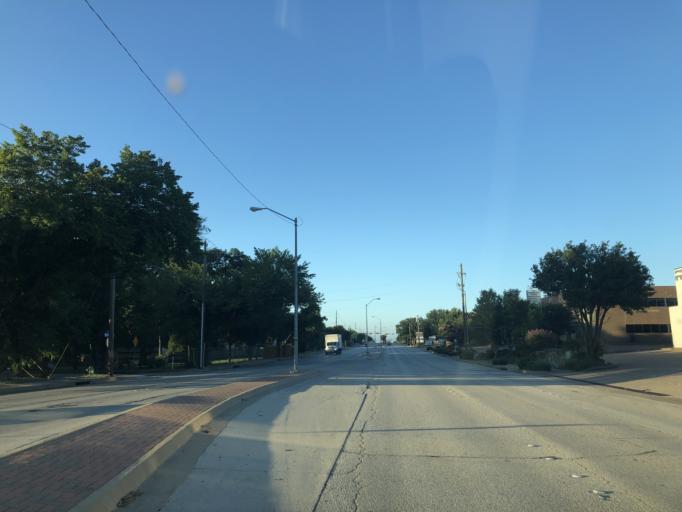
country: US
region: Texas
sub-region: Dallas County
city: Duncanville
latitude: 32.6580
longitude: -96.9258
